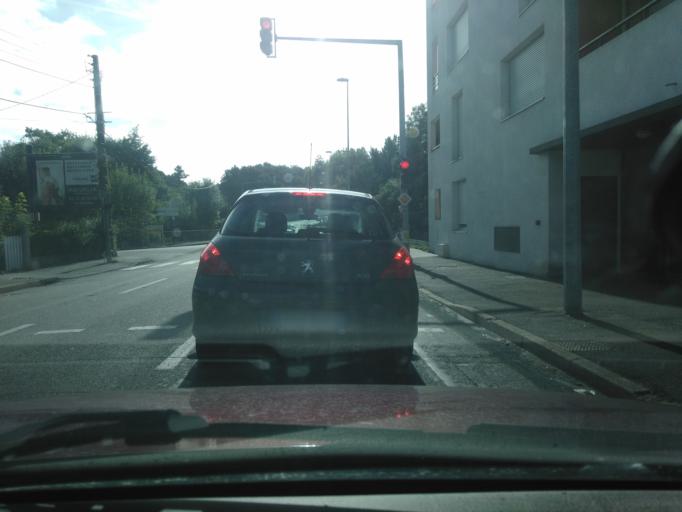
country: FR
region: Pays de la Loire
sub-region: Departement de la Vendee
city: La Roche-sur-Yon
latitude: 46.6707
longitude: -1.4163
